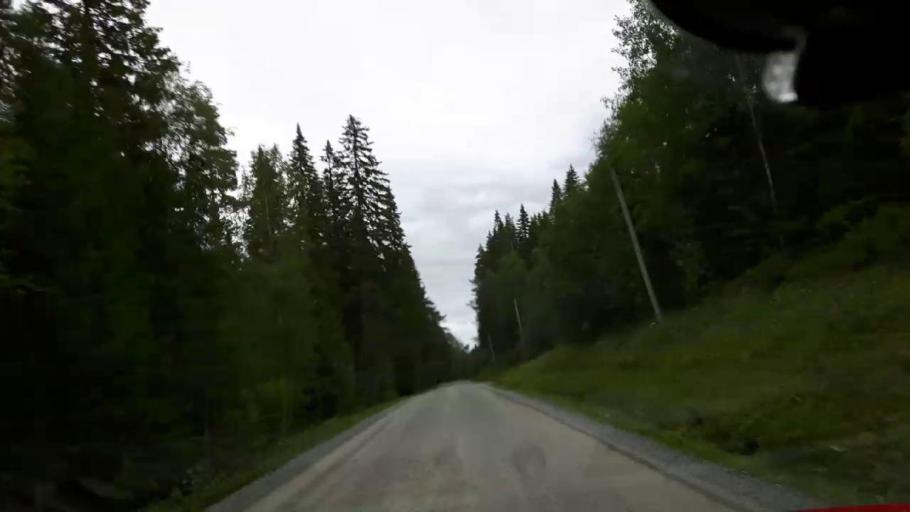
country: SE
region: Jaemtland
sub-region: Braecke Kommun
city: Braecke
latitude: 63.0894
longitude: 15.2584
